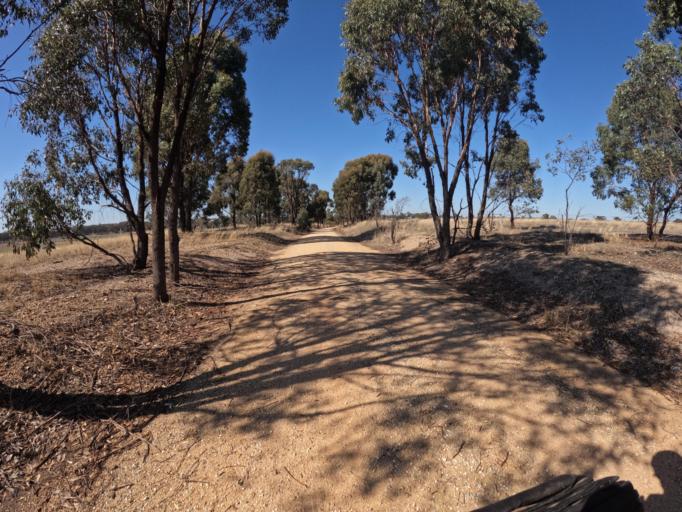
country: AU
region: Victoria
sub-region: Greater Bendigo
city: Kennington
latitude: -36.8206
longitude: 144.5775
